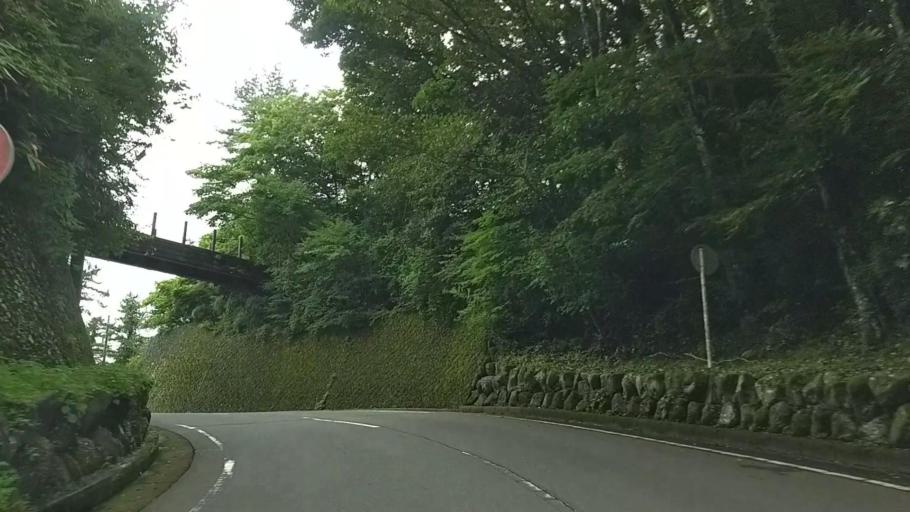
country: JP
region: Shizuoka
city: Gotemba
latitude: 35.3199
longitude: 139.0126
